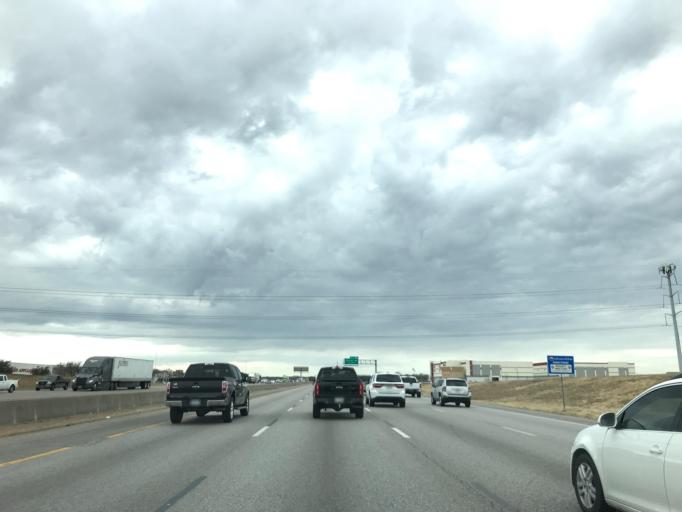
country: US
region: Texas
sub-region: Tarrant County
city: Arlington
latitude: 32.6766
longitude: -97.0812
